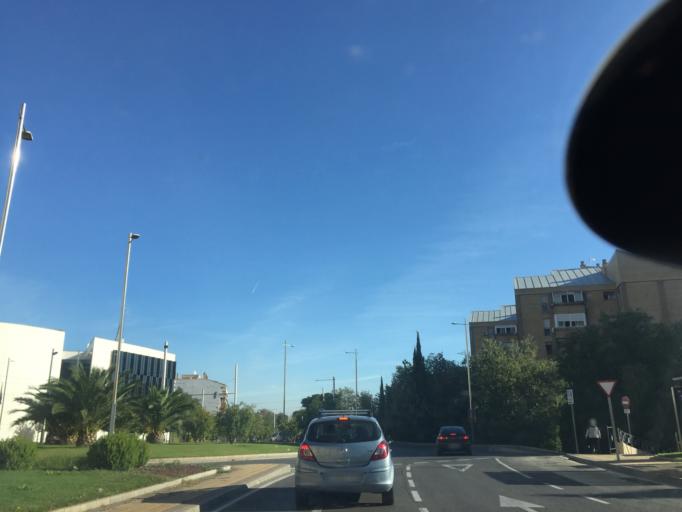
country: ES
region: Andalusia
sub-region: Provincia de Jaen
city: Jaen
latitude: 37.7793
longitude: -3.7849
